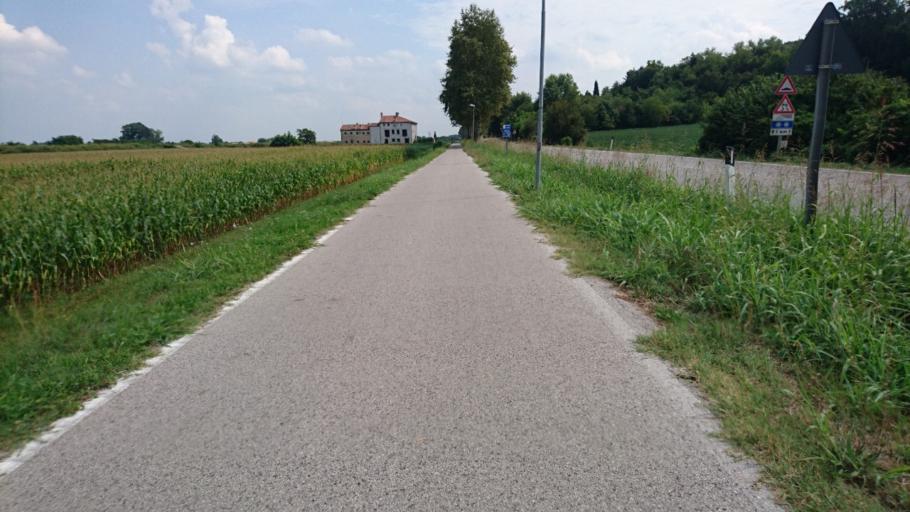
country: IT
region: Veneto
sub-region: Provincia di Vicenza
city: Longare
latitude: 45.4928
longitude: 11.5926
